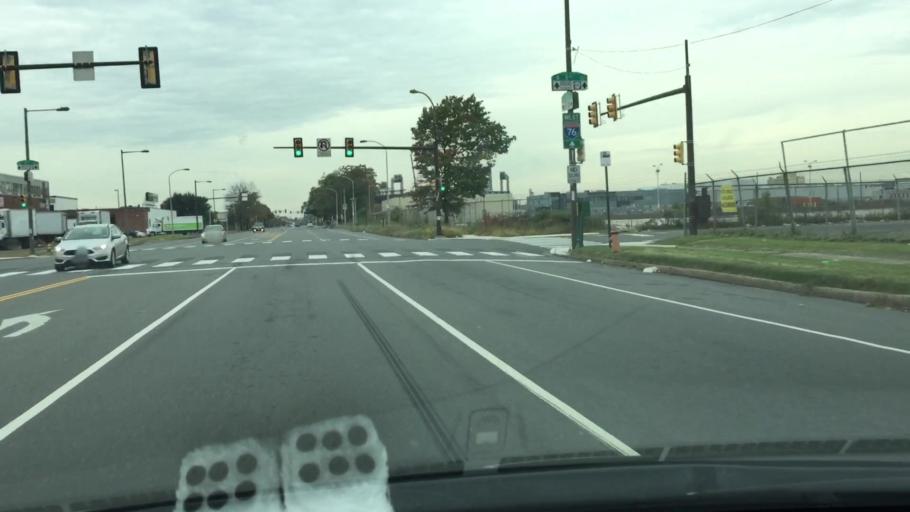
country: US
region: New Jersey
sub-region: Camden County
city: Gloucester City
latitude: 39.9030
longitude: -75.1543
